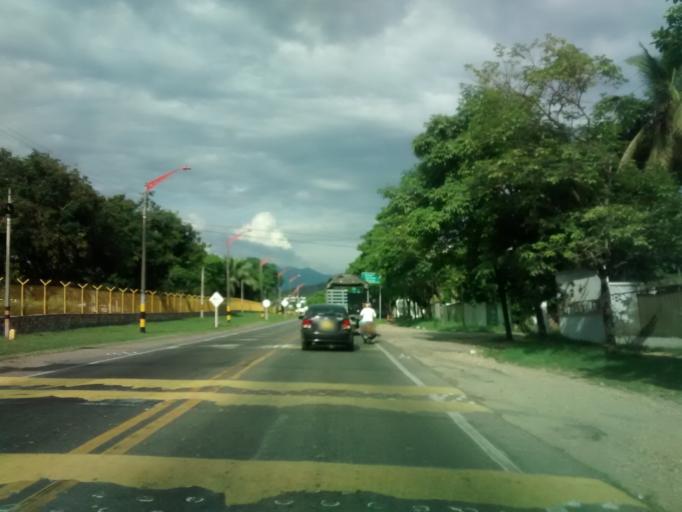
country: CO
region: Tolima
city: Melgar
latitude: 4.2133
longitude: -74.6312
